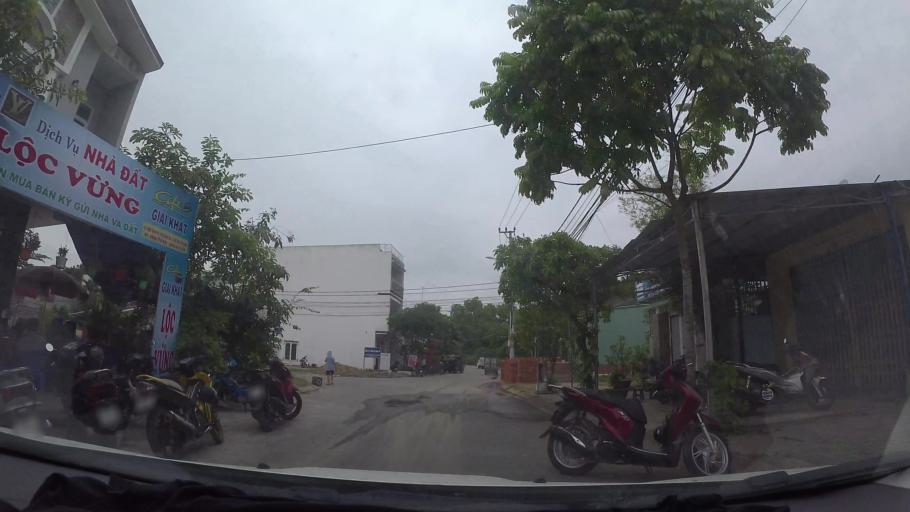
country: VN
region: Da Nang
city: Lien Chieu
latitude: 16.0667
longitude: 108.1443
